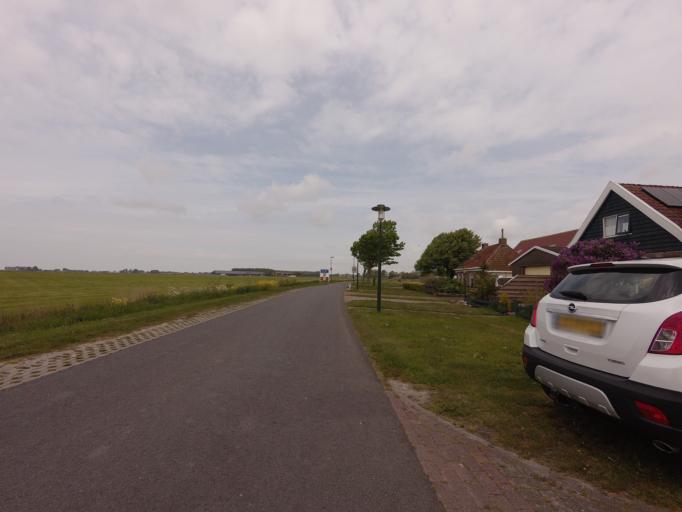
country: NL
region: Friesland
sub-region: Sudwest Fryslan
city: Bolsward
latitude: 53.0844
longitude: 5.4827
